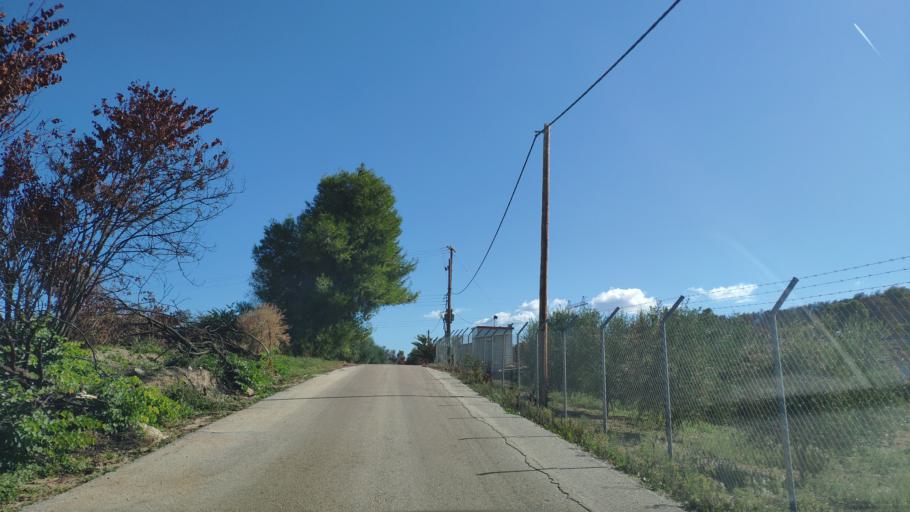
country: GR
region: Peloponnese
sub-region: Nomos Korinthias
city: Athikia
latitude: 37.8446
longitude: 22.9385
